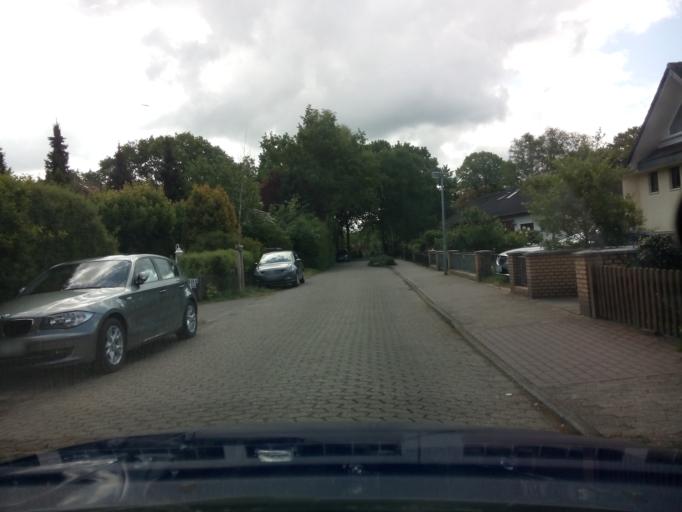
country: DE
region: Lower Saxony
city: Lilienthal
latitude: 53.1345
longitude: 8.9124
